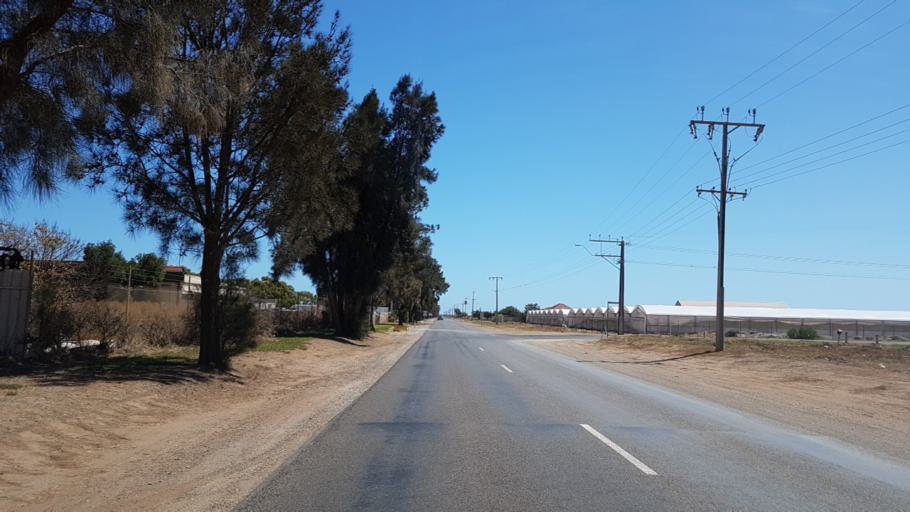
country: AU
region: South Australia
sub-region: Playford
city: Virginia
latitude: -34.7282
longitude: 138.5650
